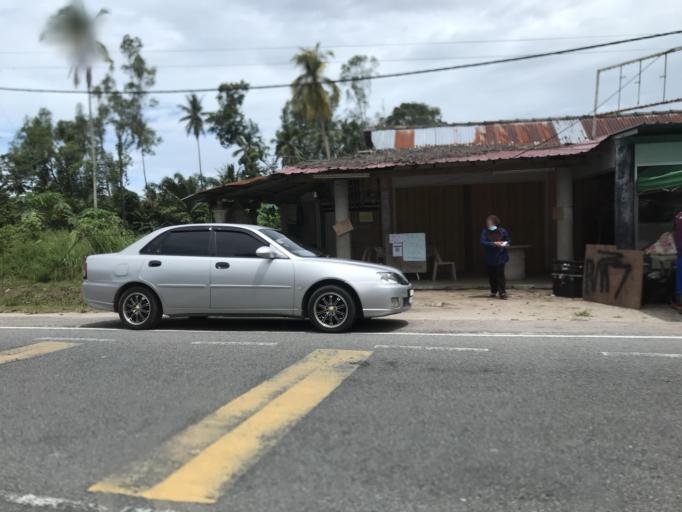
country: MY
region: Kelantan
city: Tumpat
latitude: 6.1756
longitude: 102.1816
